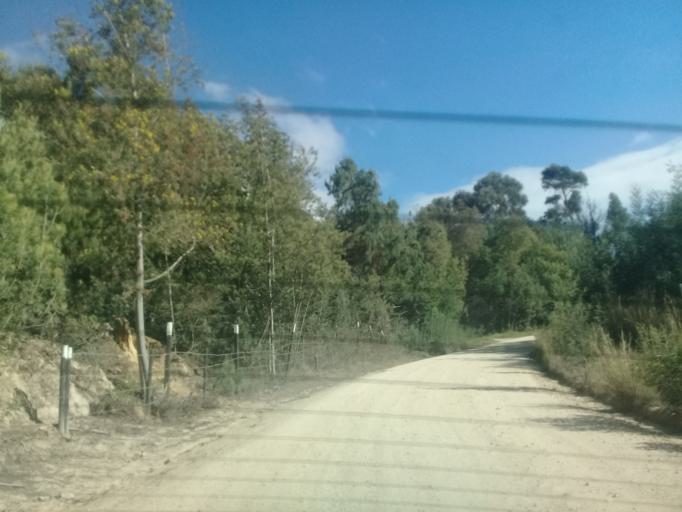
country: CO
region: Cundinamarca
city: Tocancipa
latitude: 4.9308
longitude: -73.8815
